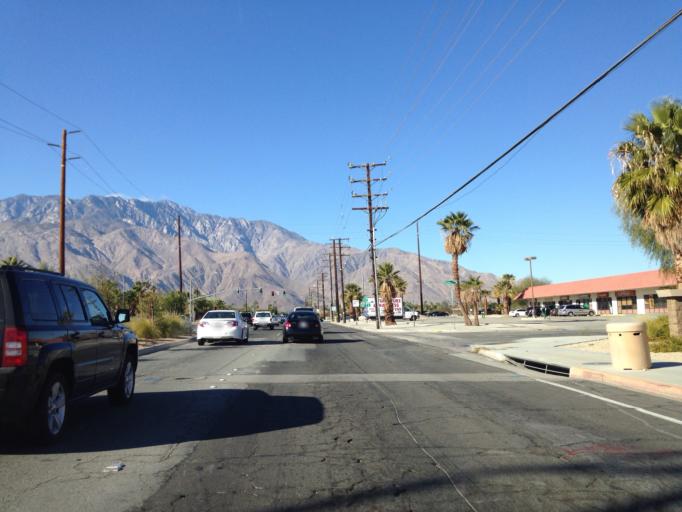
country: US
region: California
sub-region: Riverside County
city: Palm Springs
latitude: 33.8450
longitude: -116.5042
